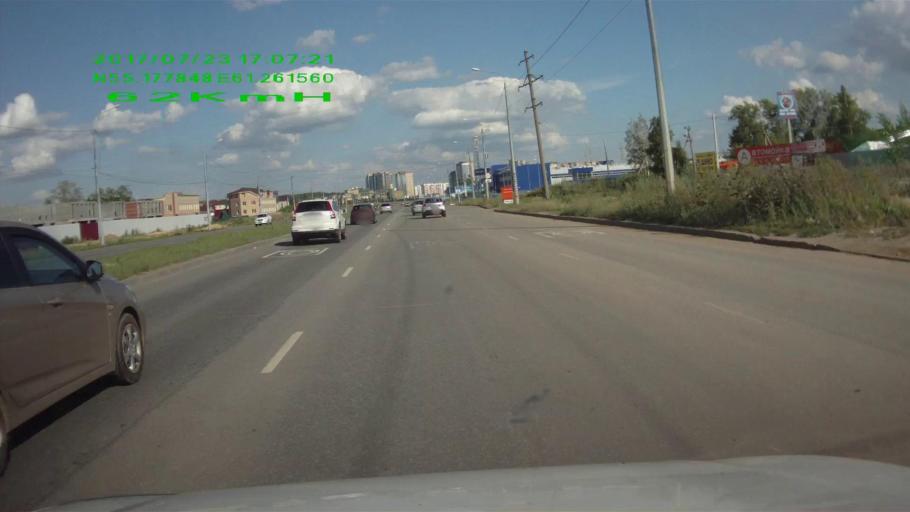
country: RU
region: Chelyabinsk
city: Roshchino
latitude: 55.1776
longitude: 61.2625
